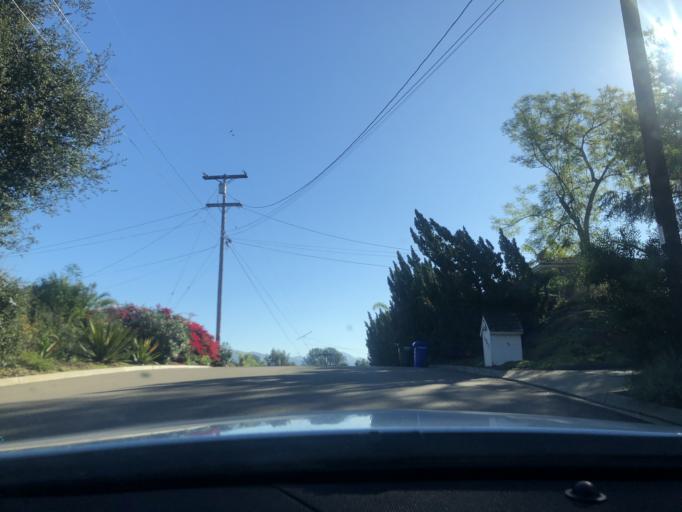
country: US
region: California
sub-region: San Diego County
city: Rancho San Diego
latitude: 32.7681
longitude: -116.9435
